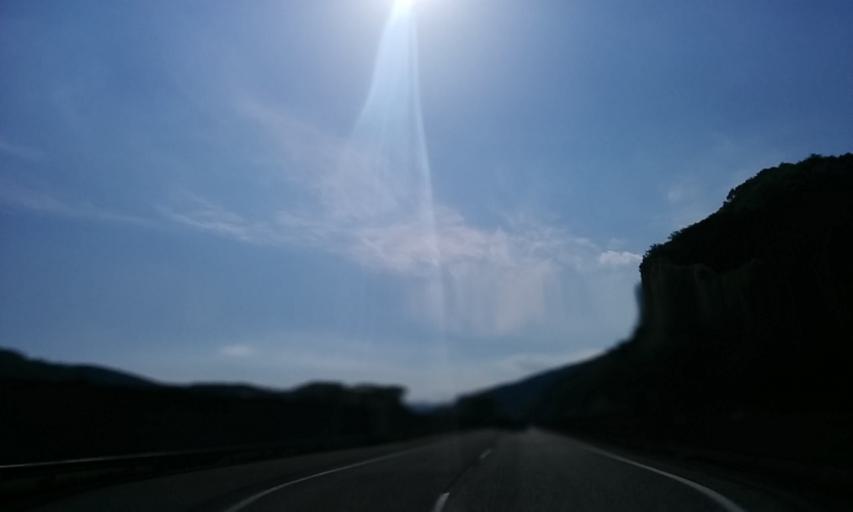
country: JP
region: Shiga Prefecture
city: Nagahama
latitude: 35.3340
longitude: 136.3702
